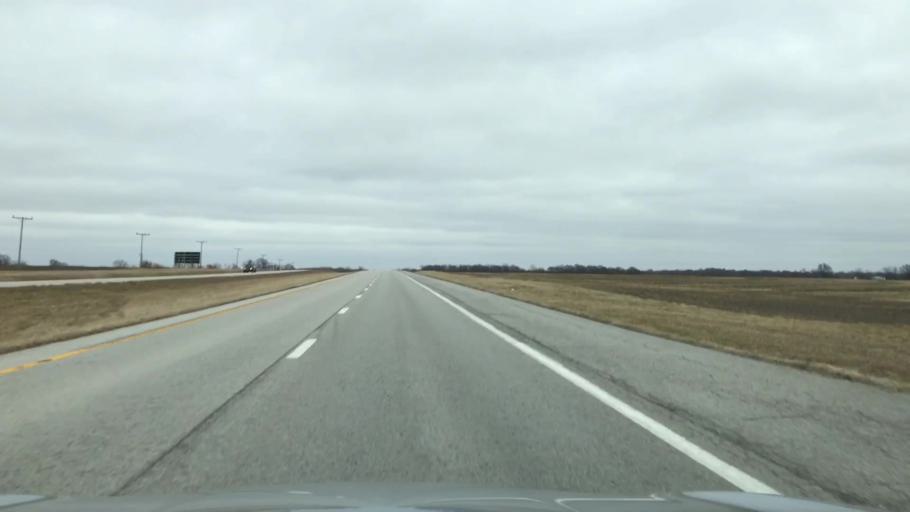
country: US
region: Missouri
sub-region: Livingston County
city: Chillicothe
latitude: 39.7763
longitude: -93.4628
